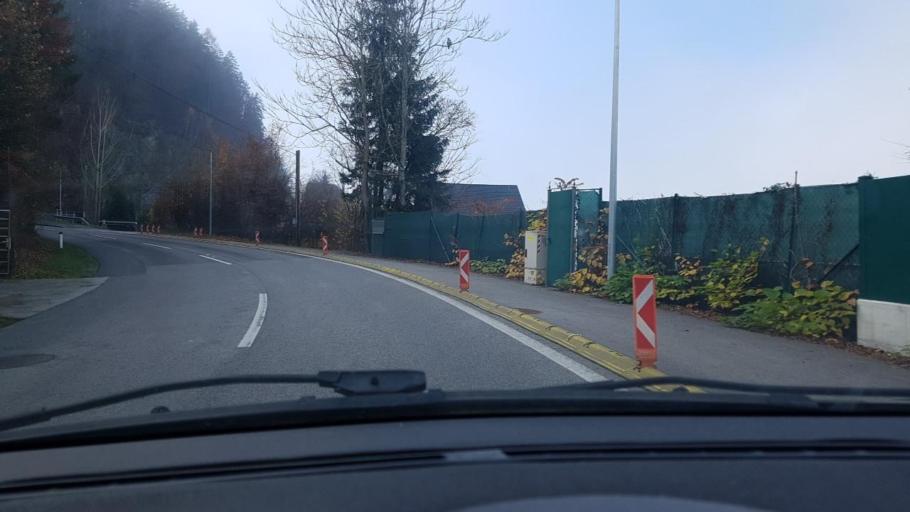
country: AT
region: Carinthia
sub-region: Politischer Bezirk Klagenfurt Land
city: Kottmannsdorf
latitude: 46.6128
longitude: 14.2399
